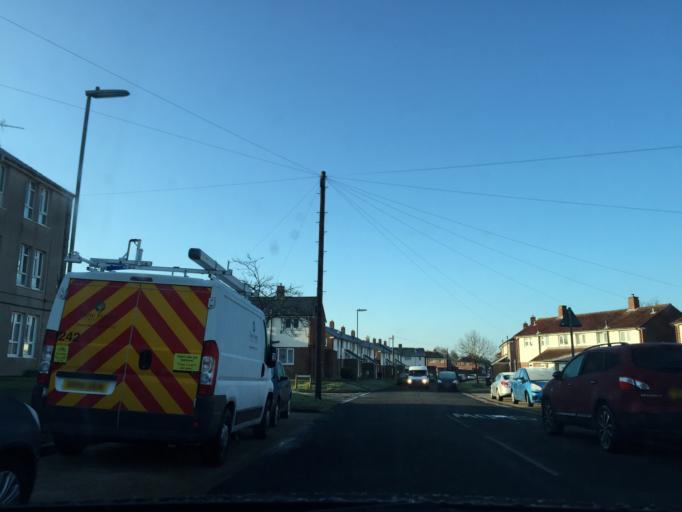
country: GB
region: England
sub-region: Hampshire
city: Lee-on-the-Solent
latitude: 50.8146
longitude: -1.1686
